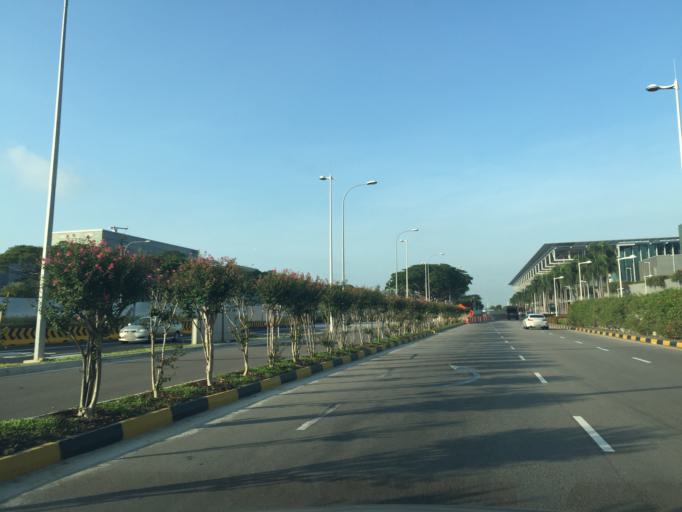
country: SG
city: Singapore
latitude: 1.3588
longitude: 103.9888
